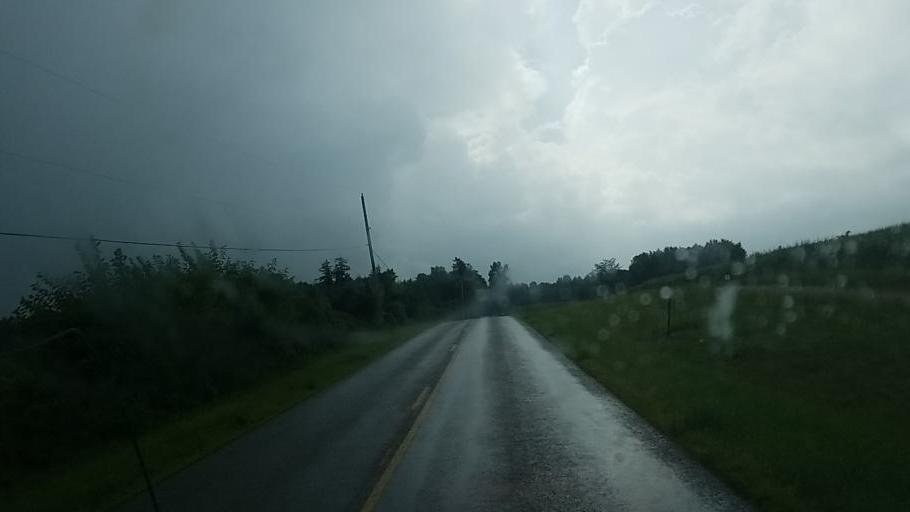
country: US
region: Ohio
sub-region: Champaign County
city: North Lewisburg
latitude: 40.3185
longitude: -83.6027
